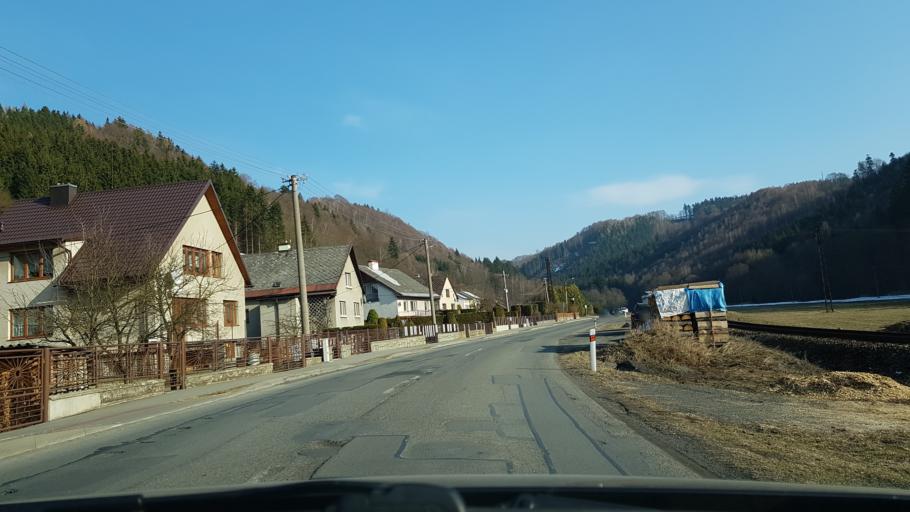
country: CZ
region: Olomoucky
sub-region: Okres Sumperk
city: Hanusovice
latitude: 50.0804
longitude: 16.9415
